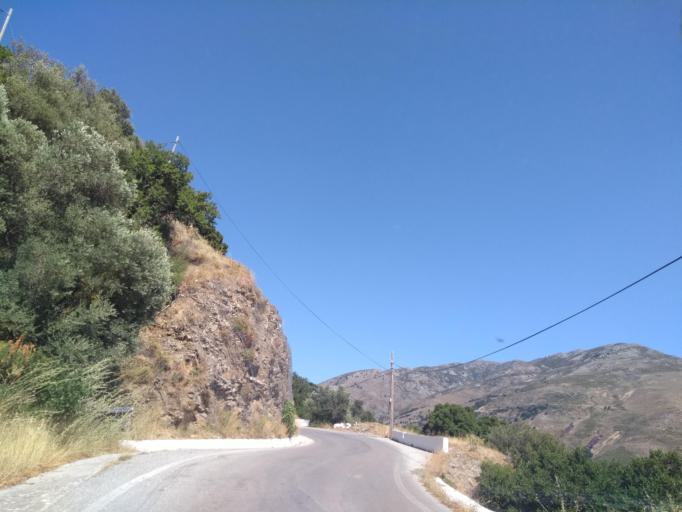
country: GR
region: Crete
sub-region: Nomos Chanias
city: Vryses
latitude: 35.3645
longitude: 23.5908
